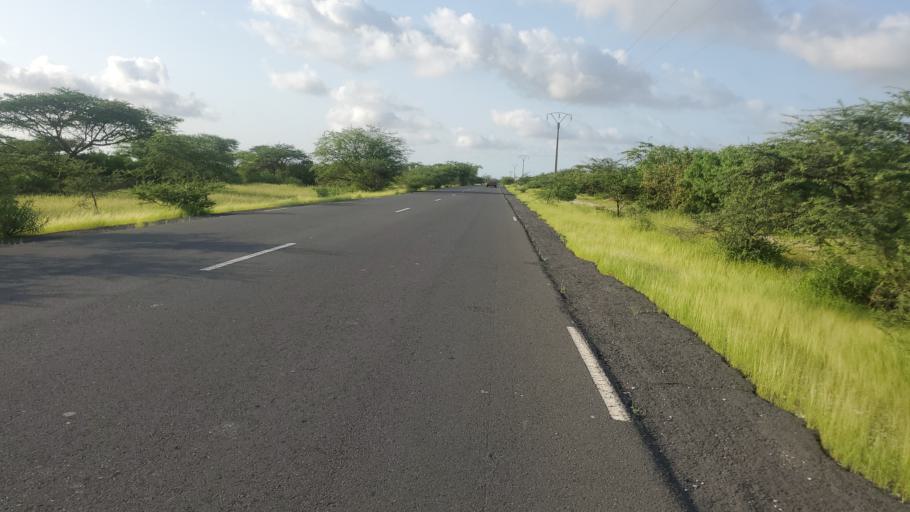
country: SN
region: Saint-Louis
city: Saint-Louis
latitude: 16.1133
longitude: -16.4132
